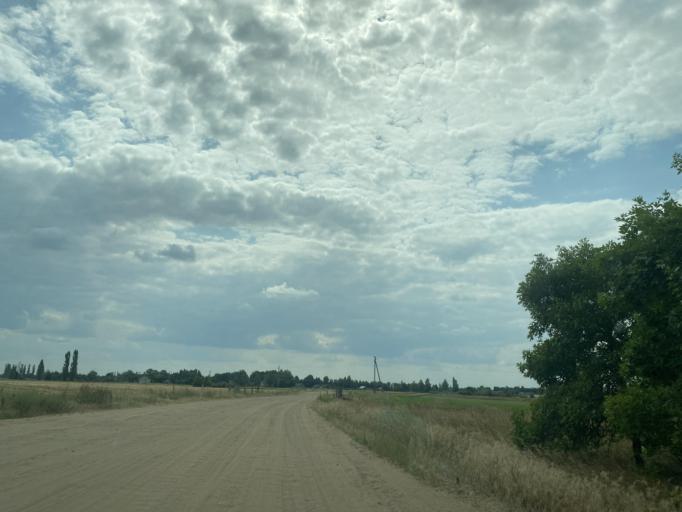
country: BY
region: Brest
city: Ivanava
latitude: 52.3574
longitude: 25.6317
